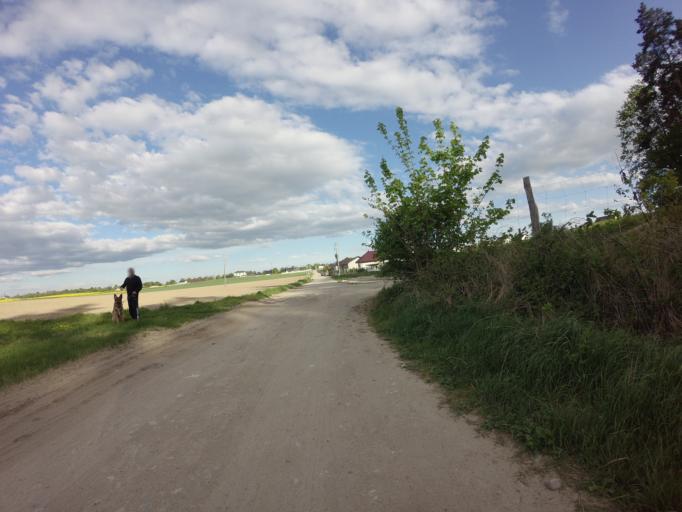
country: PL
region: West Pomeranian Voivodeship
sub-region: Powiat choszczenski
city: Choszczno
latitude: 53.1605
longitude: 15.3846
